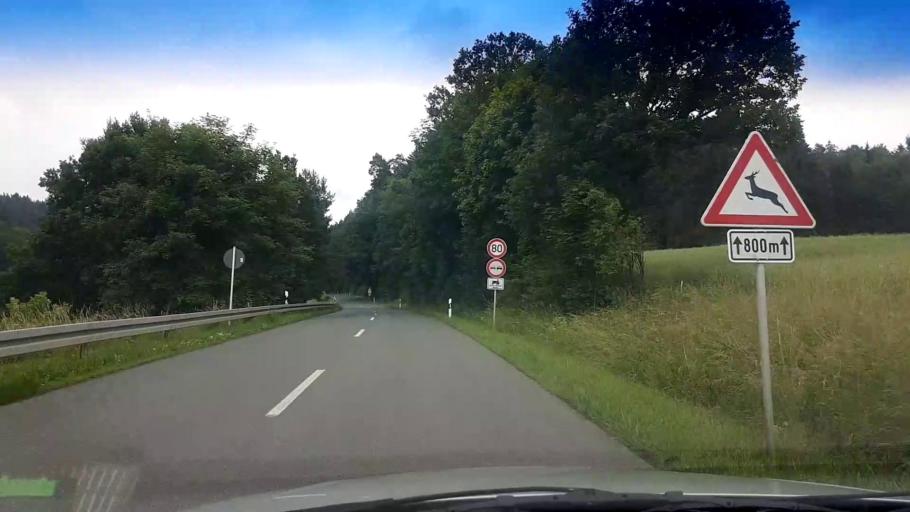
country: DE
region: Bavaria
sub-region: Upper Franconia
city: Kasendorf
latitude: 50.0743
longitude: 11.3273
